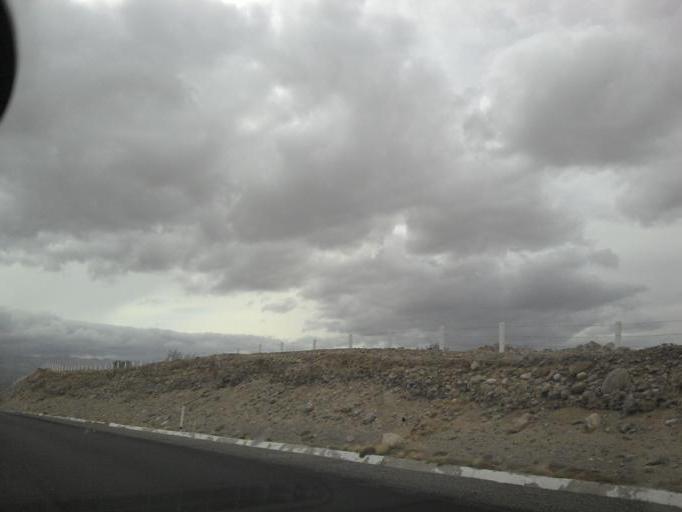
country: MX
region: Baja California
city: Progreso
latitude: 32.5645
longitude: -115.8733
